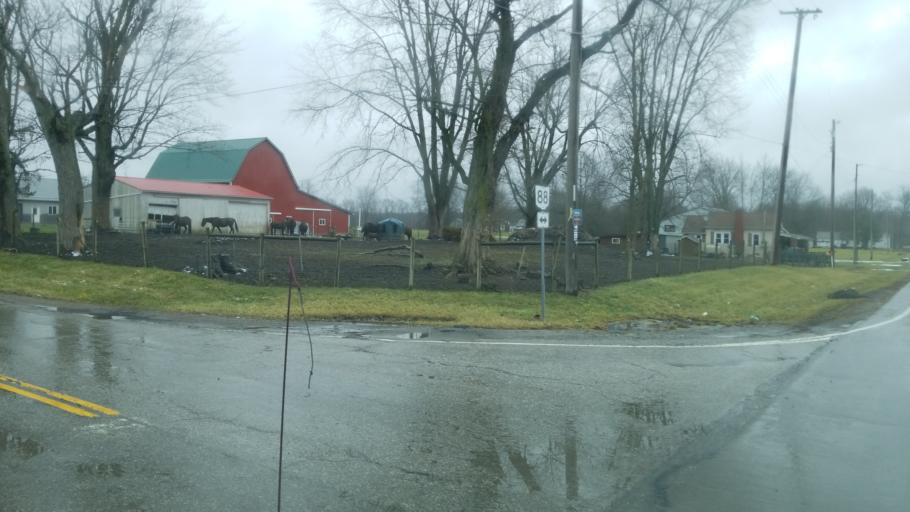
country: US
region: Ohio
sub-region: Geauga County
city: Middlefield
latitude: 41.3905
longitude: -80.9547
